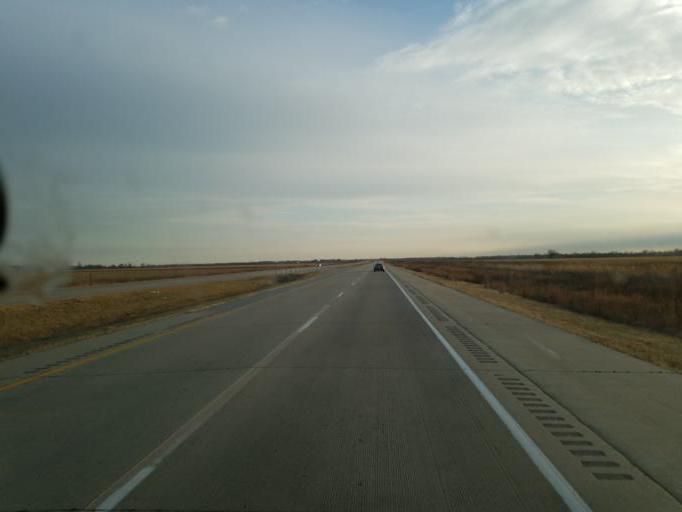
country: US
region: Iowa
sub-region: Monona County
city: Onawa
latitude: 41.8770
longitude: -96.1044
